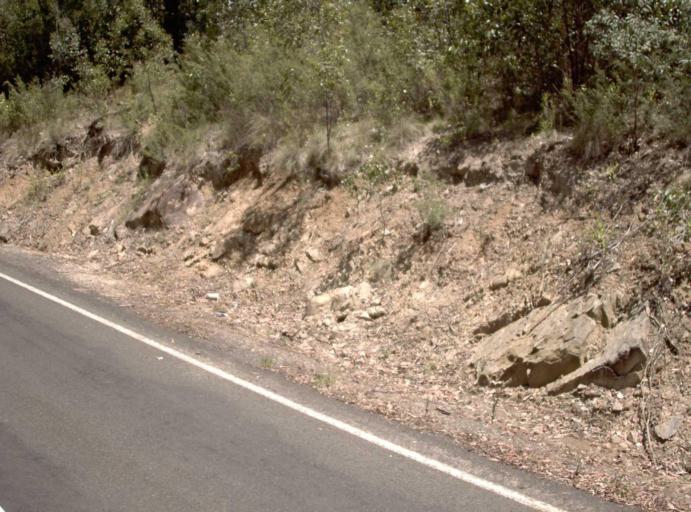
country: AU
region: Victoria
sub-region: East Gippsland
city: Lakes Entrance
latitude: -37.6216
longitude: 147.8829
